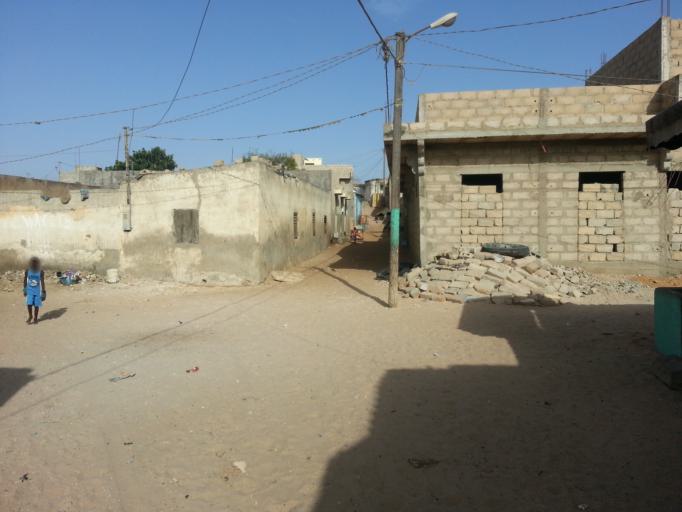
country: SN
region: Dakar
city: Pikine
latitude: 14.7727
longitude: -17.3801
